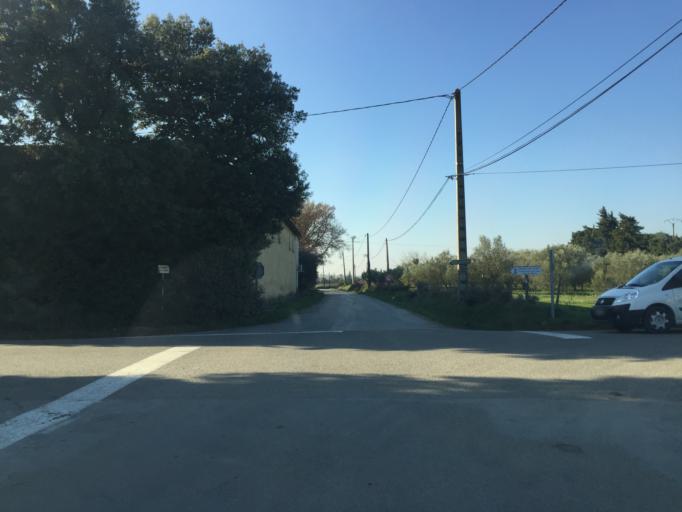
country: FR
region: Provence-Alpes-Cote d'Azur
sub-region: Departement du Vaucluse
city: Courthezon
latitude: 44.0820
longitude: 4.9077
